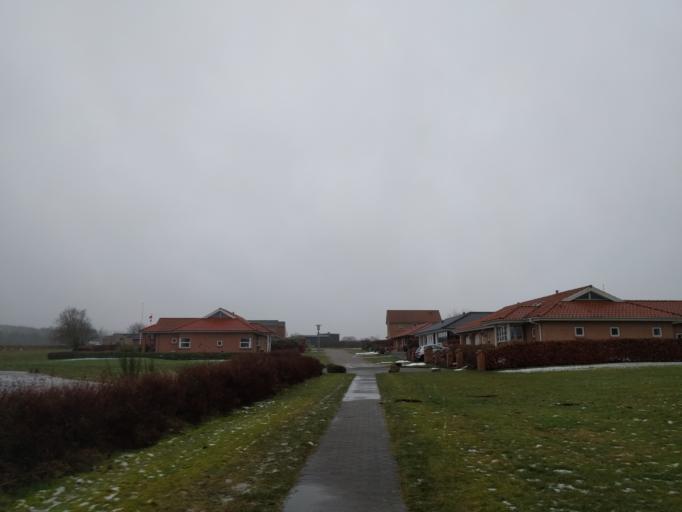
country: DK
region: Central Jutland
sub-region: Viborg Kommune
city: Viborg
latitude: 56.4294
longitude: 9.4081
